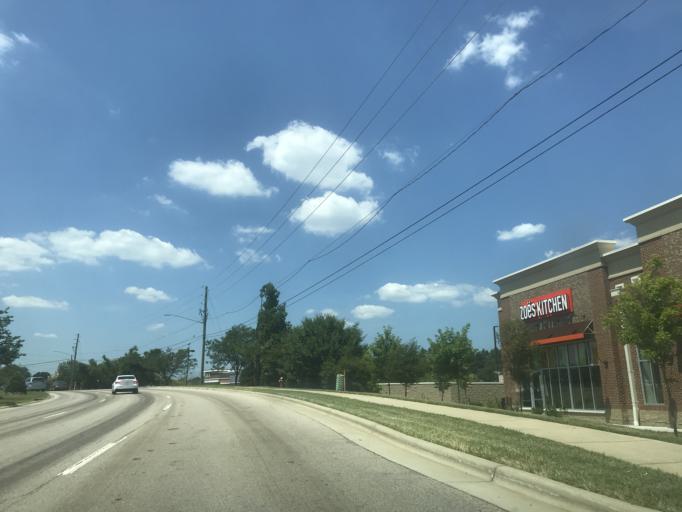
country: US
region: North Carolina
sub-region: Wake County
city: Cary
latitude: 35.7576
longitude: -78.7415
